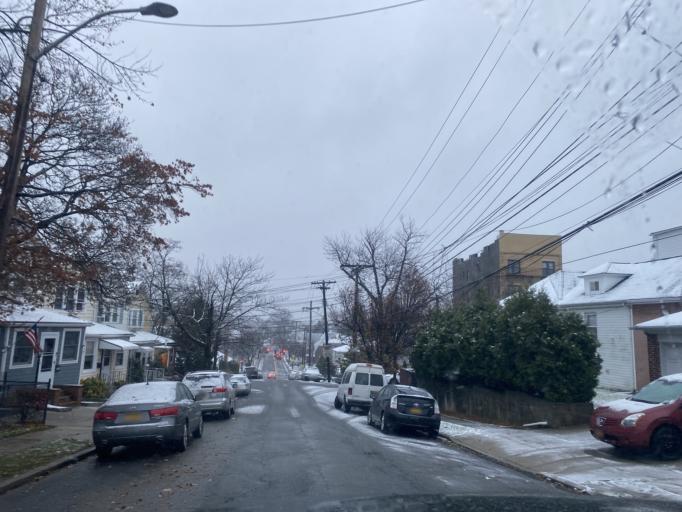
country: US
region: New York
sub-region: Westchester County
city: Mount Vernon
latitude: 40.9068
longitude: -73.8646
